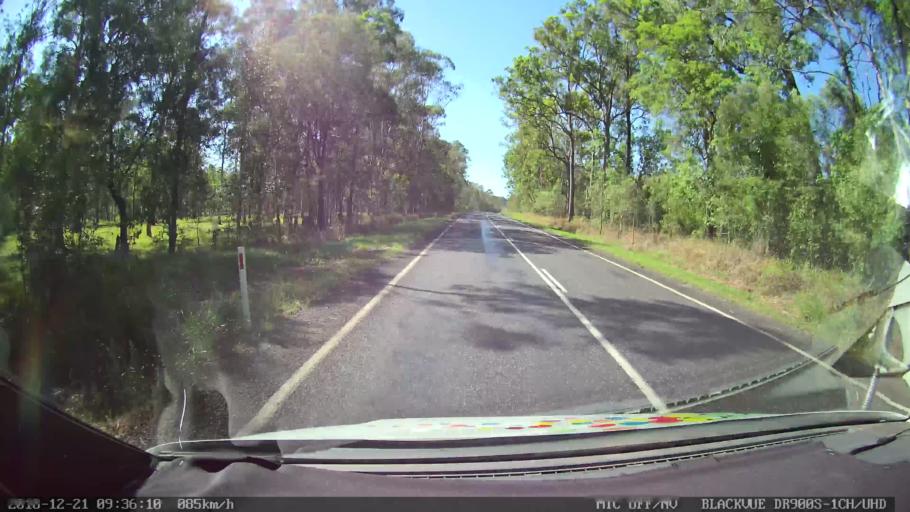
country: AU
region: New South Wales
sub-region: Clarence Valley
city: Grafton
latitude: -29.5200
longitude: 152.9821
